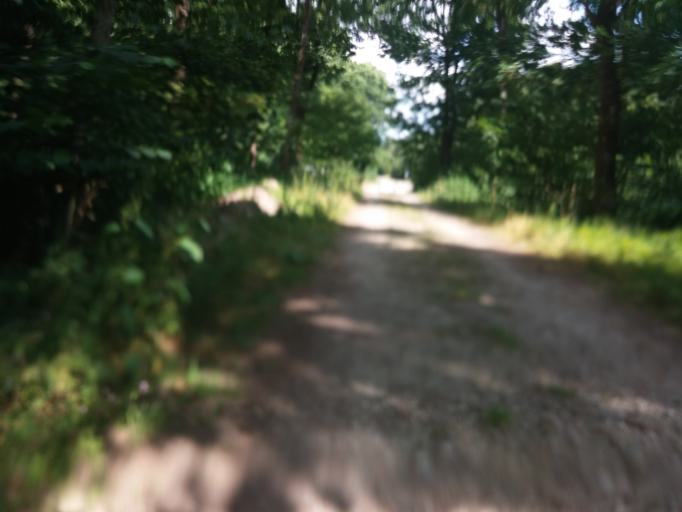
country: DE
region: Bavaria
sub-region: Upper Bavaria
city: Unterhaching
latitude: 48.0836
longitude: 11.6006
